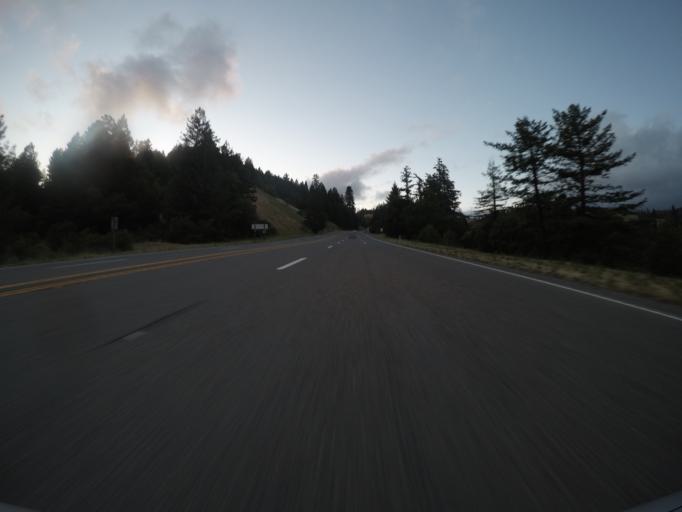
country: US
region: California
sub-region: Humboldt County
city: Redway
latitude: 40.0686
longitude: -123.7891
